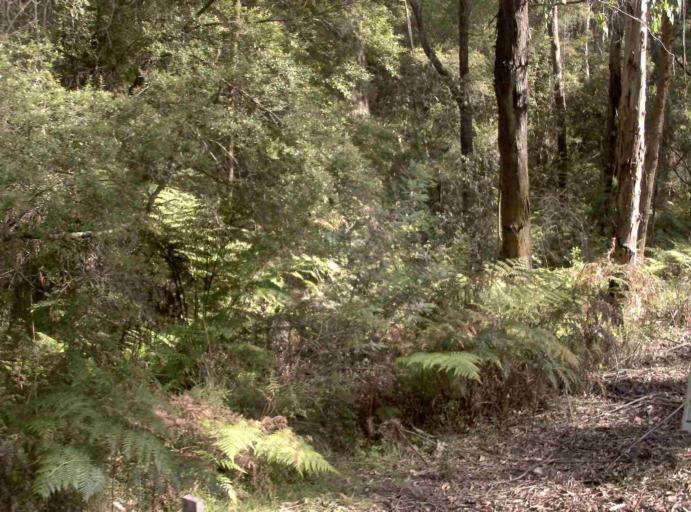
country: AU
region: Victoria
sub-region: East Gippsland
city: Lakes Entrance
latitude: -37.4663
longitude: 148.5627
